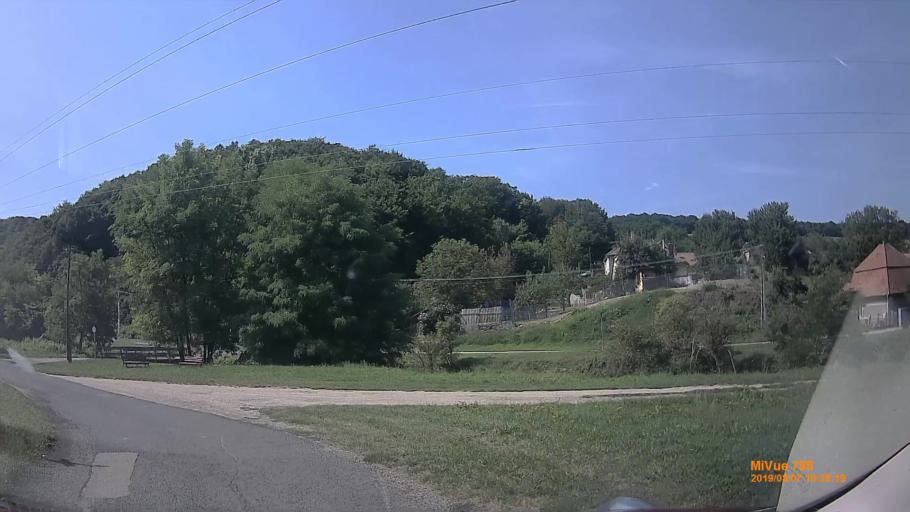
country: HU
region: Veszprem
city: Ajka
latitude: 47.0851
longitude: 17.5722
